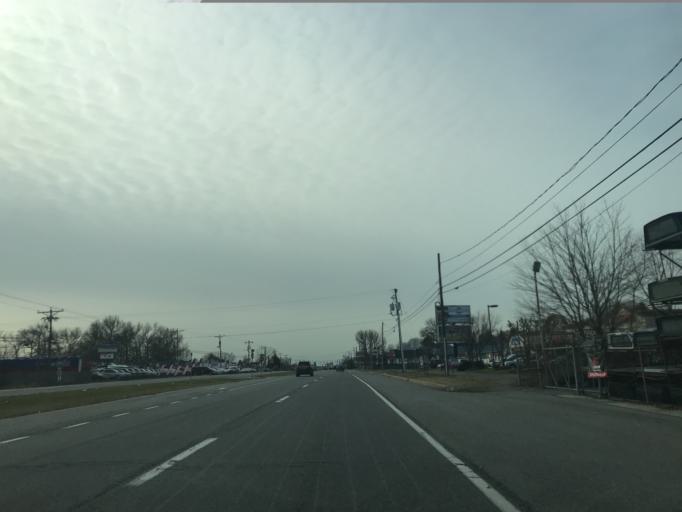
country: US
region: Delaware
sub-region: New Castle County
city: Bear
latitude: 39.6426
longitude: -75.6434
